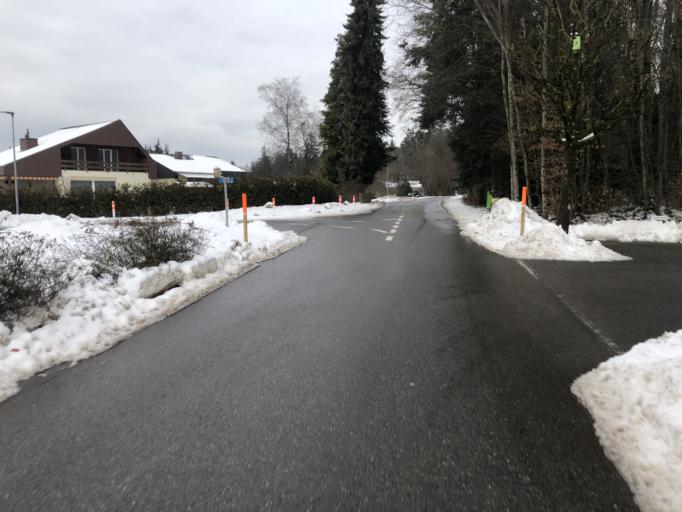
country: CH
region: Bern
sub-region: Oberaargau
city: Lotzwil
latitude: 47.2015
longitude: 7.7622
